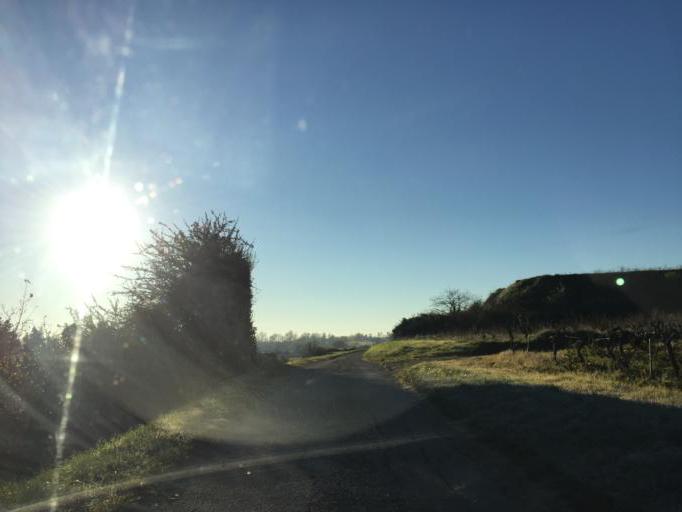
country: FR
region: Provence-Alpes-Cote d'Azur
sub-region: Departement du Vaucluse
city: Courthezon
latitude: 44.1080
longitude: 4.8776
